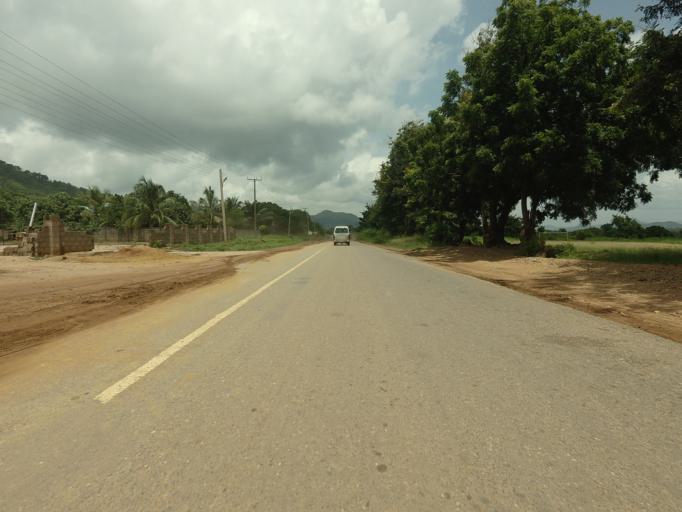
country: GH
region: Volta
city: Ho
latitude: 6.7079
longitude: 0.3345
